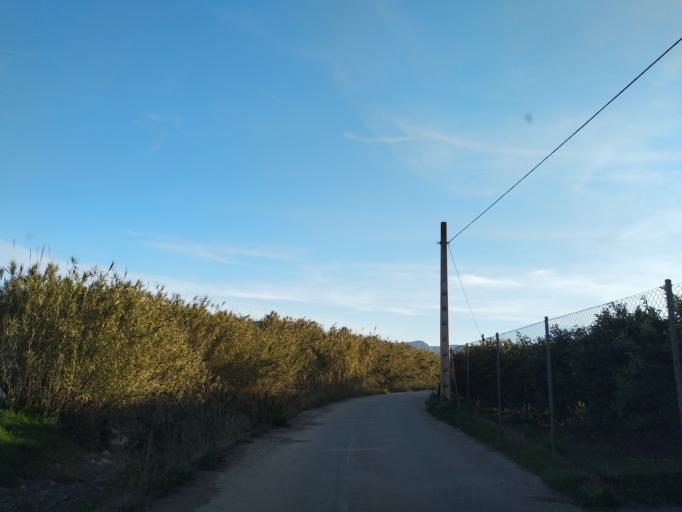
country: ES
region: Andalusia
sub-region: Provincia de Malaga
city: Estacion de Cartama
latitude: 36.7314
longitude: -4.5779
